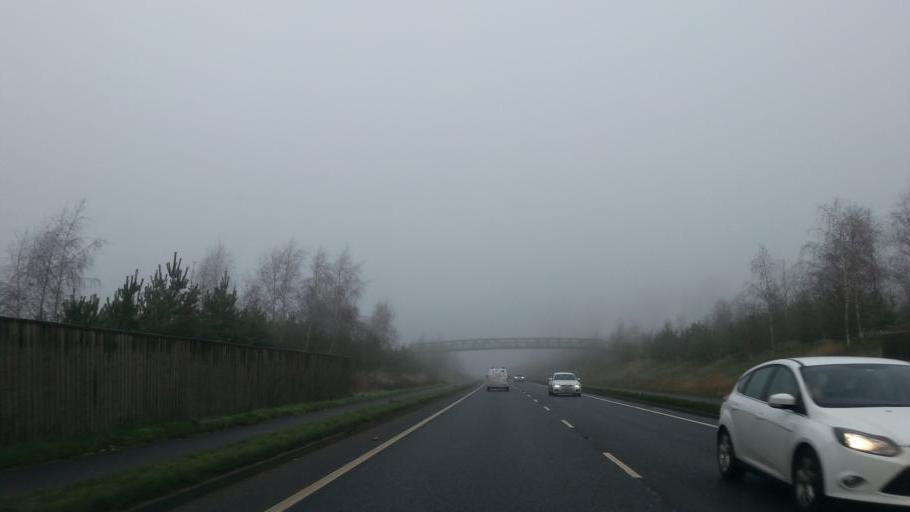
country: GB
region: England
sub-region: Cheshire East
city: Alderley Edge
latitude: 53.2777
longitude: -2.2429
